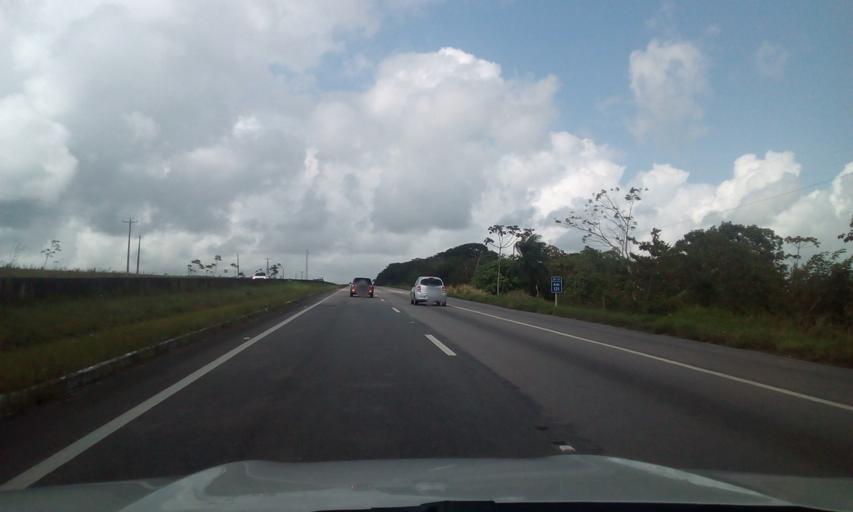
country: BR
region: Paraiba
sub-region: Alhandra
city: Alhandra
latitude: -7.4424
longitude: -34.9782
